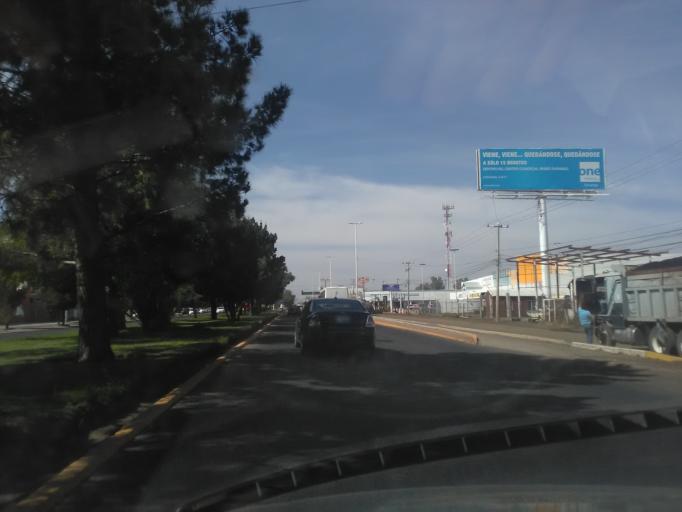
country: MX
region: Durango
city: Victoria de Durango
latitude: 24.0591
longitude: -104.6104
